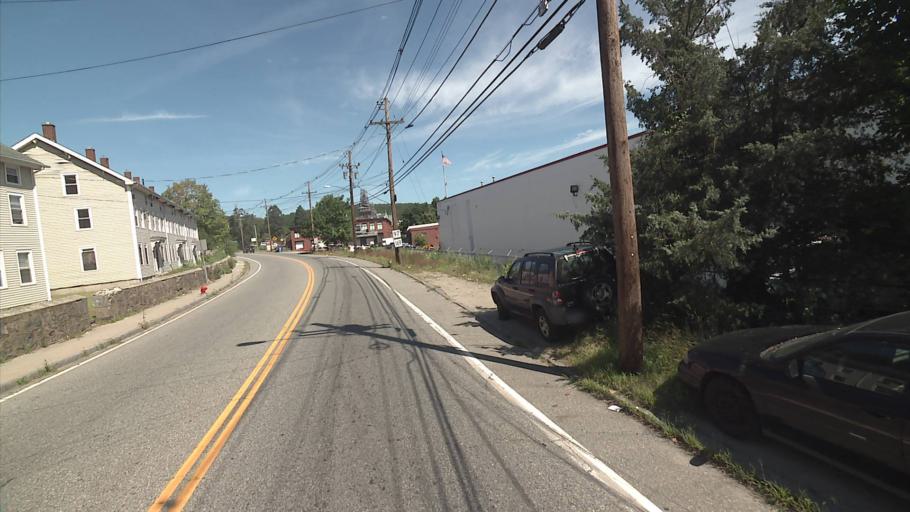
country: US
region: Connecticut
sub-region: New London County
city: Lisbon
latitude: 41.5663
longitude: -72.0460
